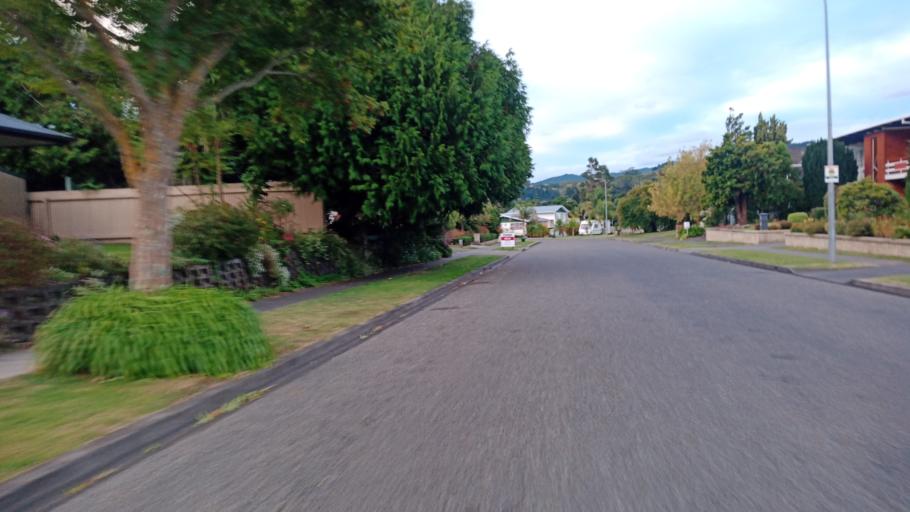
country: NZ
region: Gisborne
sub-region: Gisborne District
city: Gisborne
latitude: -38.6508
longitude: 178.0083
